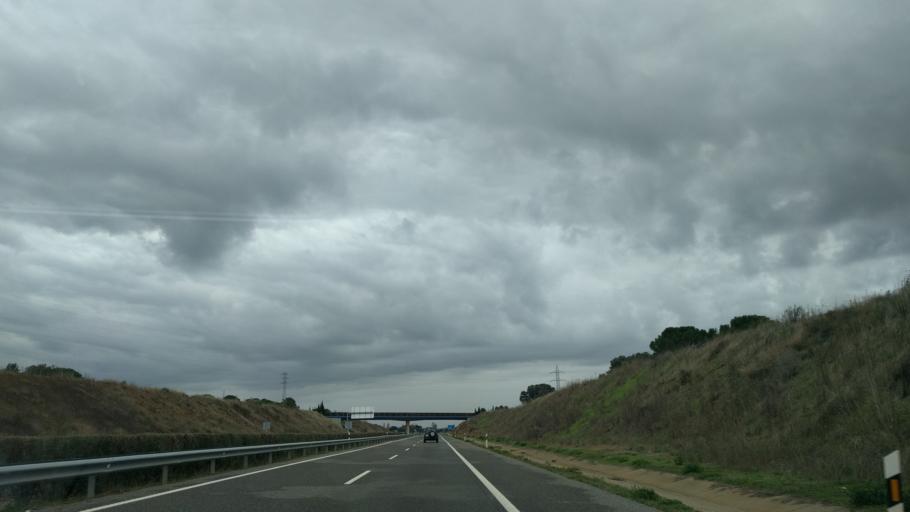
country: ES
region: Aragon
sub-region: Provincia de Huesca
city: Castejon del Puente
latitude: 41.9478
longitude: 0.1906
